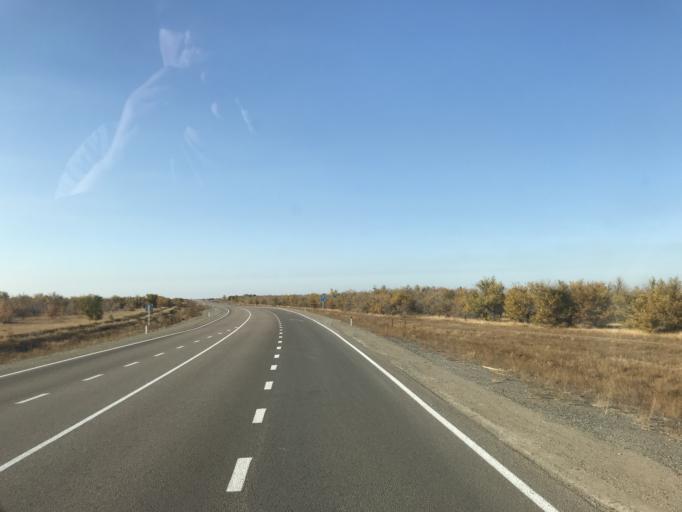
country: KZ
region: Pavlodar
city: Koktobe
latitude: 51.7290
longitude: 77.5589
